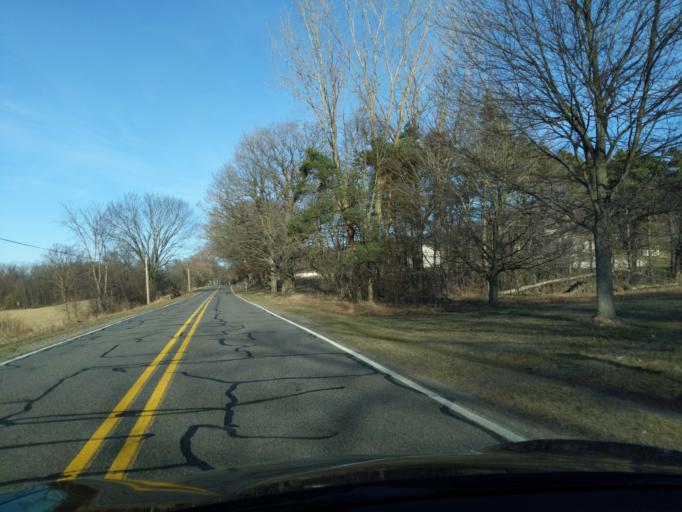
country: US
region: Michigan
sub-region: Ionia County
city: Saranac
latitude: 42.9379
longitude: -85.1859
